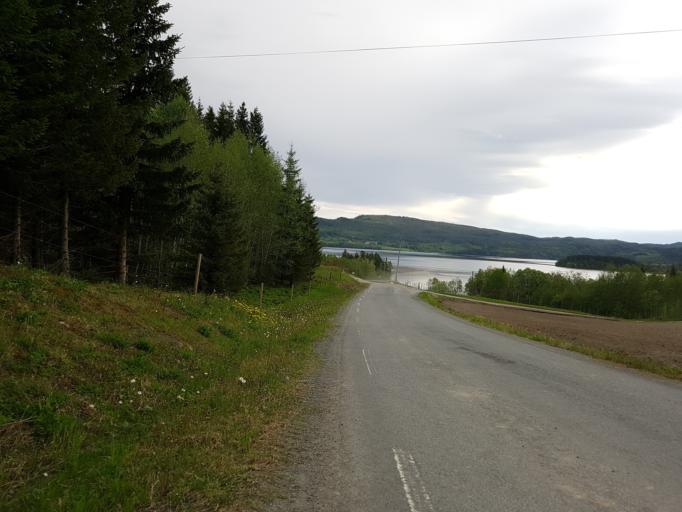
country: NO
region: Nord-Trondelag
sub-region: Levanger
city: Skogn
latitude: 63.6275
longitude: 11.2752
